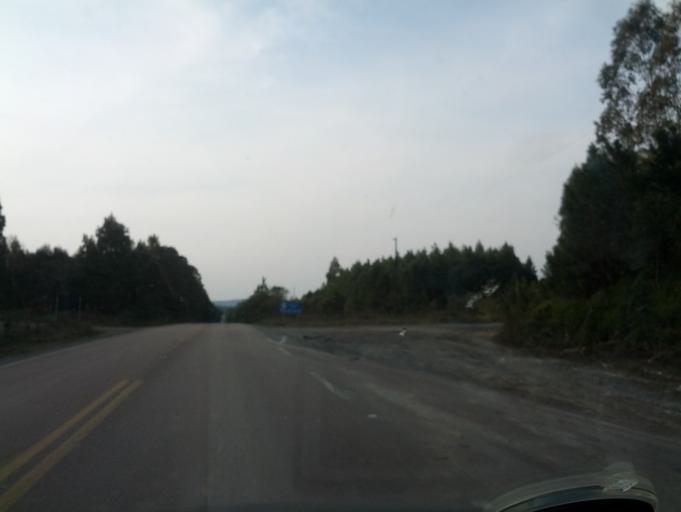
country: BR
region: Santa Catarina
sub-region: Otacilio Costa
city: Otacilio Costa
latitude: -27.3860
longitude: -50.1342
